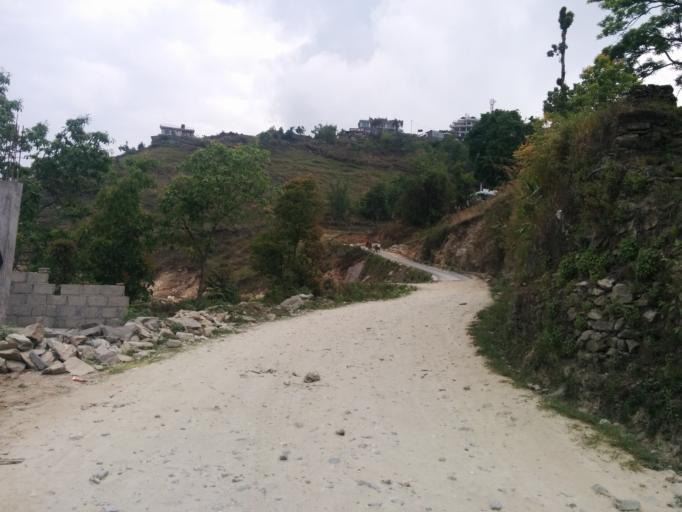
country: NP
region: Western Region
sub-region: Gandaki Zone
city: Pokhara
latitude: 28.2420
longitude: 83.9501
